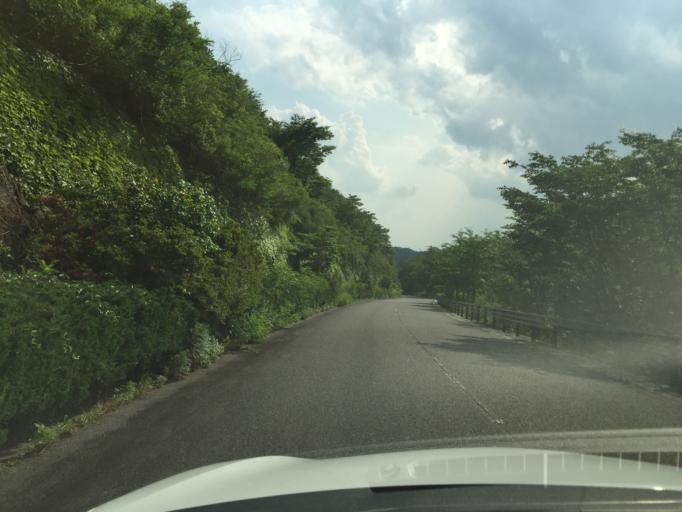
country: JP
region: Fukushima
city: Miharu
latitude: 37.4030
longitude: 140.4754
